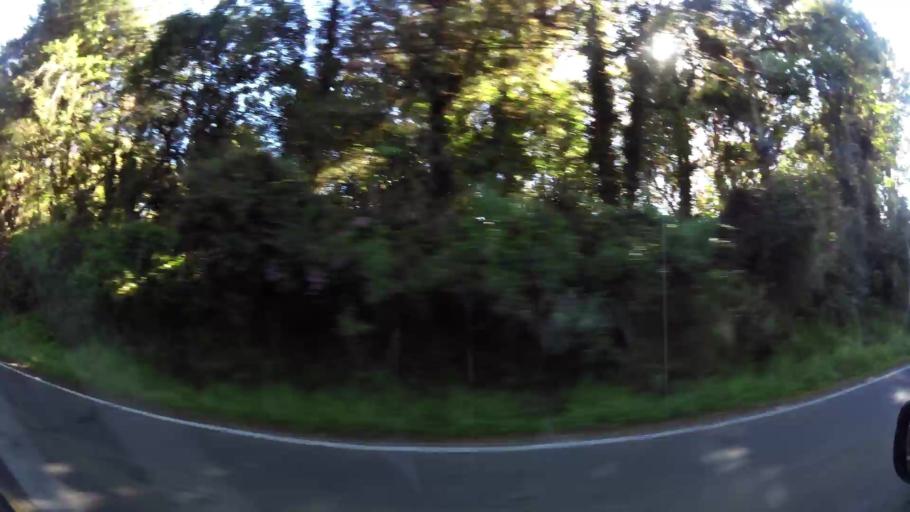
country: CR
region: San Jose
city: San Marcos
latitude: 9.6897
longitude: -83.9210
